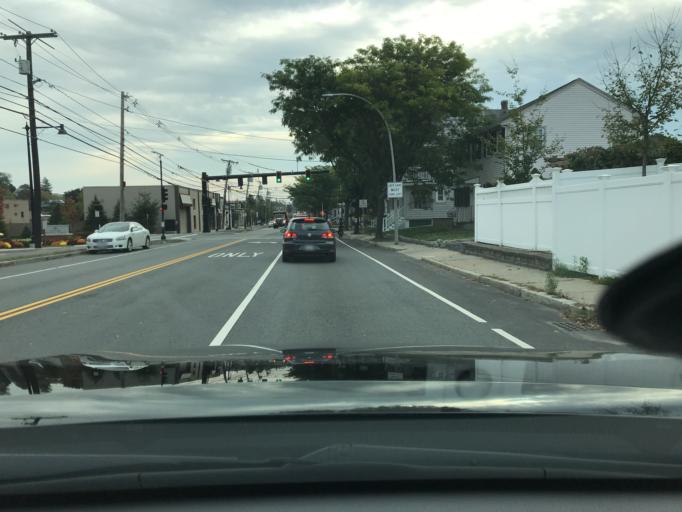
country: US
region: Massachusetts
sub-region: Middlesex County
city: Watertown
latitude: 42.3645
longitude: -71.1745
